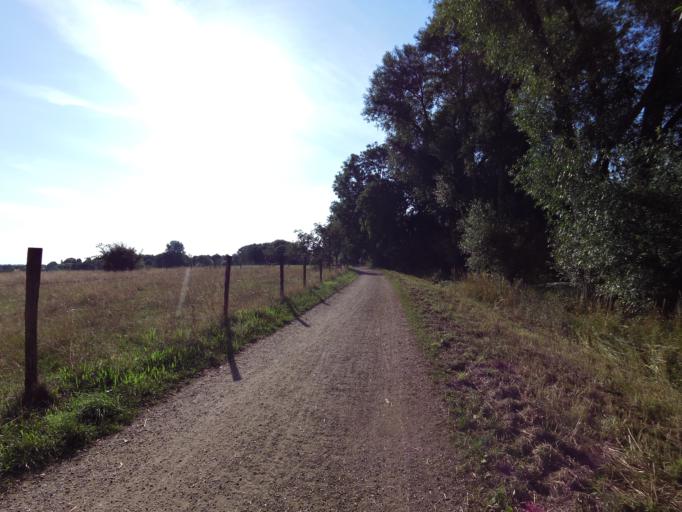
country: DE
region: North Rhine-Westphalia
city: Huckelhoven
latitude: 51.0419
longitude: 6.2131
